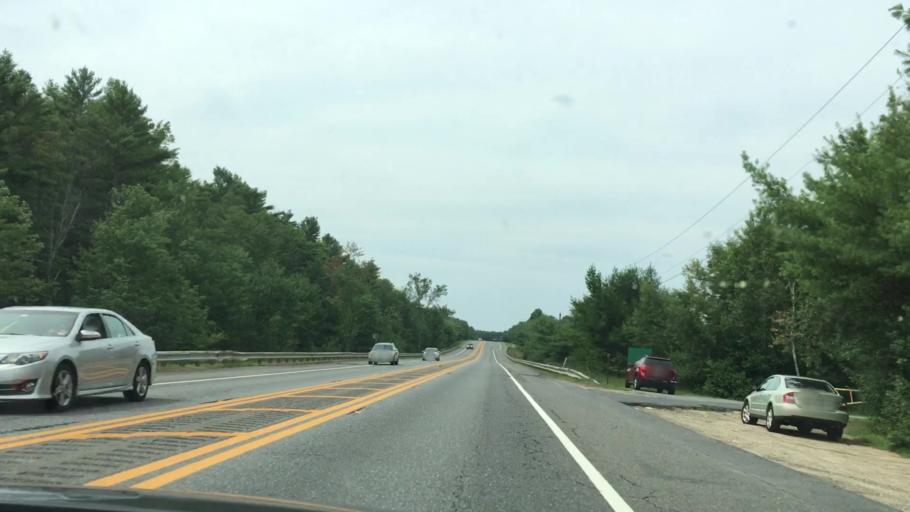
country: US
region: Massachusetts
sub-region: Worcester County
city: Gardner
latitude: 42.6085
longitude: -71.9955
